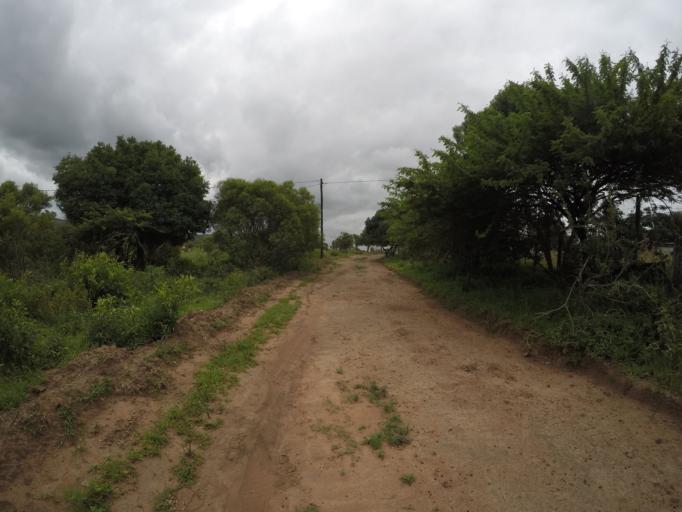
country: ZA
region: KwaZulu-Natal
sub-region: uThungulu District Municipality
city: Empangeni
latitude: -28.6029
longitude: 31.8286
